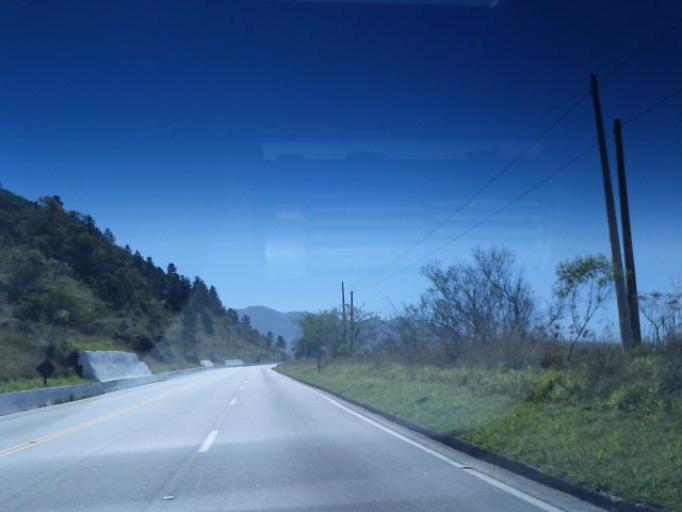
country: BR
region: Sao Paulo
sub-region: Campos Do Jordao
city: Campos do Jordao
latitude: -22.8523
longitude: -45.6153
